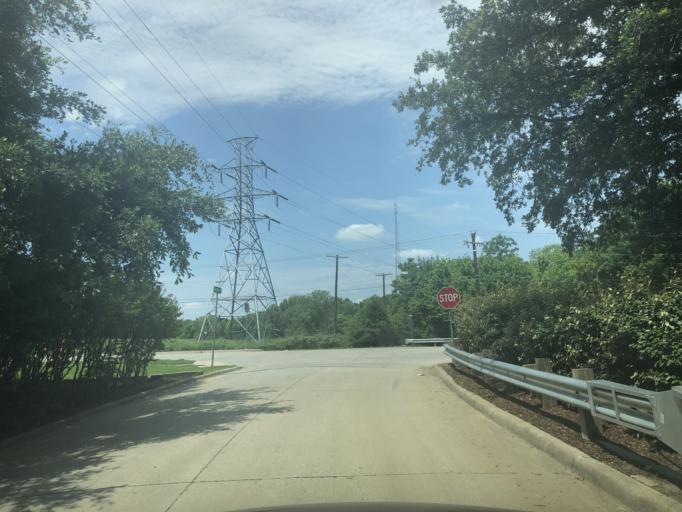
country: US
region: Texas
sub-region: Dallas County
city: Grand Prairie
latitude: 32.7238
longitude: -97.0149
